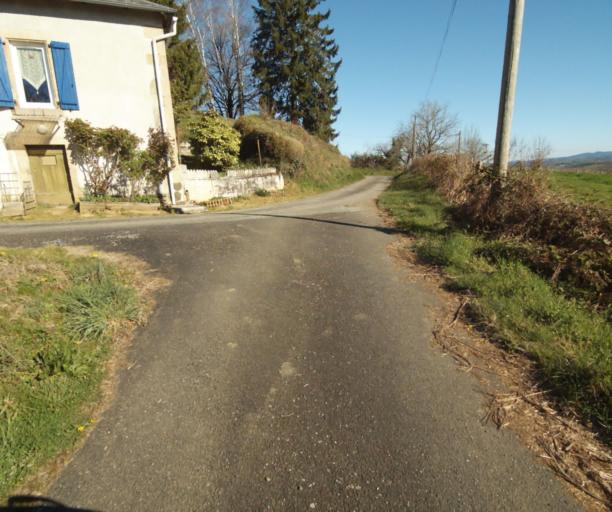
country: FR
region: Limousin
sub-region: Departement de la Correze
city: Chamboulive
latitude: 45.4029
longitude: 1.7170
